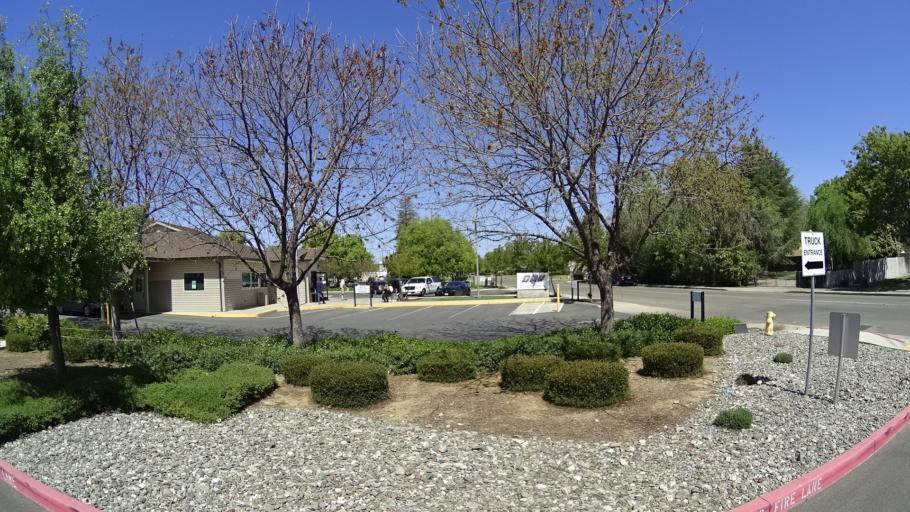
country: US
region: California
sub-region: Glenn County
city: Willows
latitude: 39.5294
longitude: -122.2123
